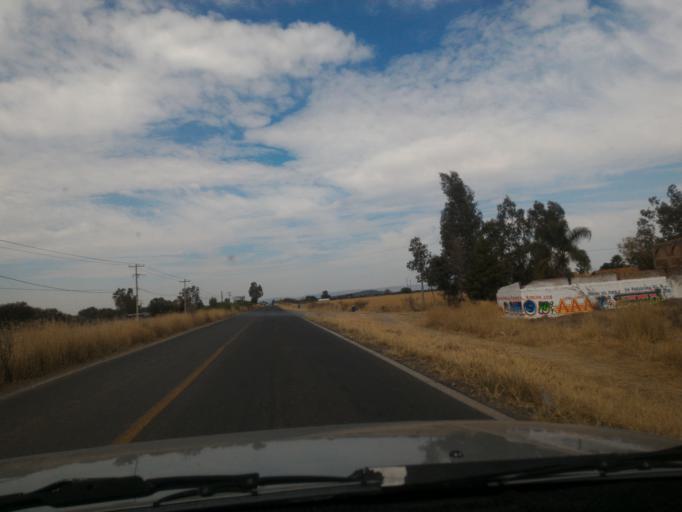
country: MX
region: Guanajuato
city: Ciudad Manuel Doblado
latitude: 20.7575
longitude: -101.9659
